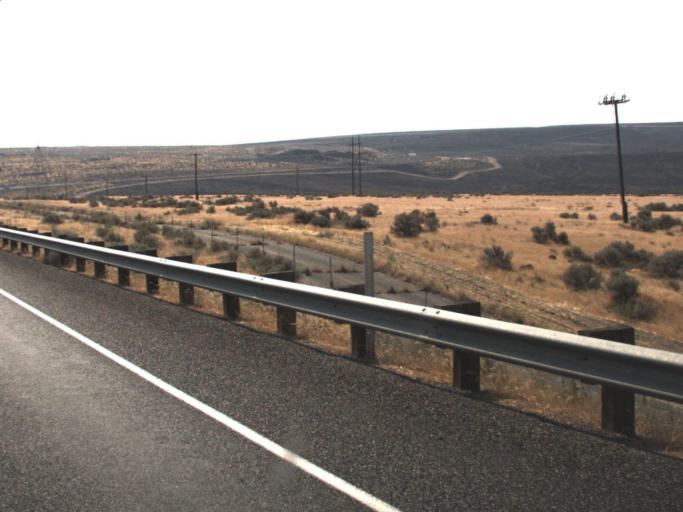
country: US
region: Washington
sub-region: Grant County
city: Desert Aire
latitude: 46.6196
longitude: -119.7266
